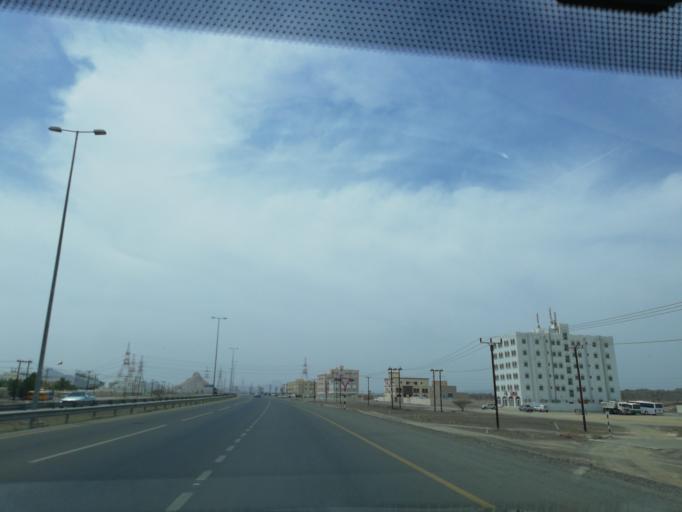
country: OM
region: Muhafazat ad Dakhiliyah
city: Nizwa
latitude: 22.8593
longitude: 57.5161
